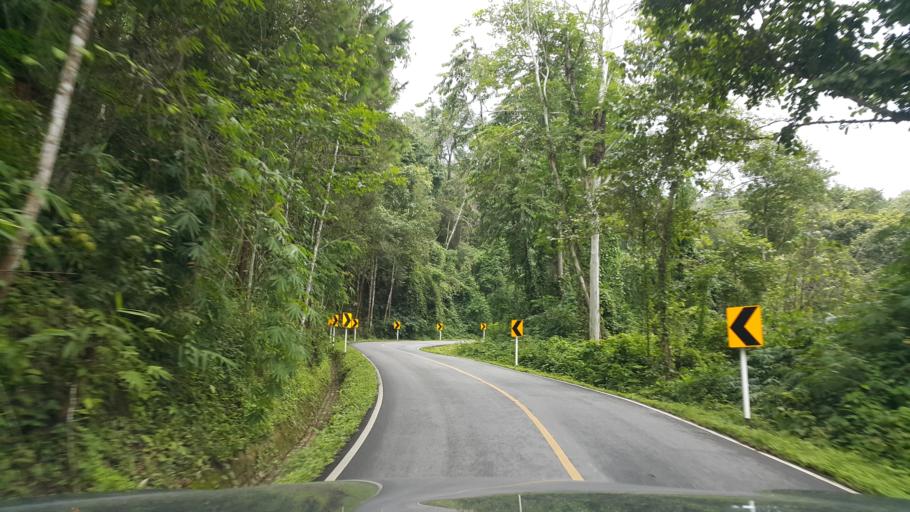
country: TH
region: Chiang Mai
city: Samoeng
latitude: 18.8653
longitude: 98.6336
